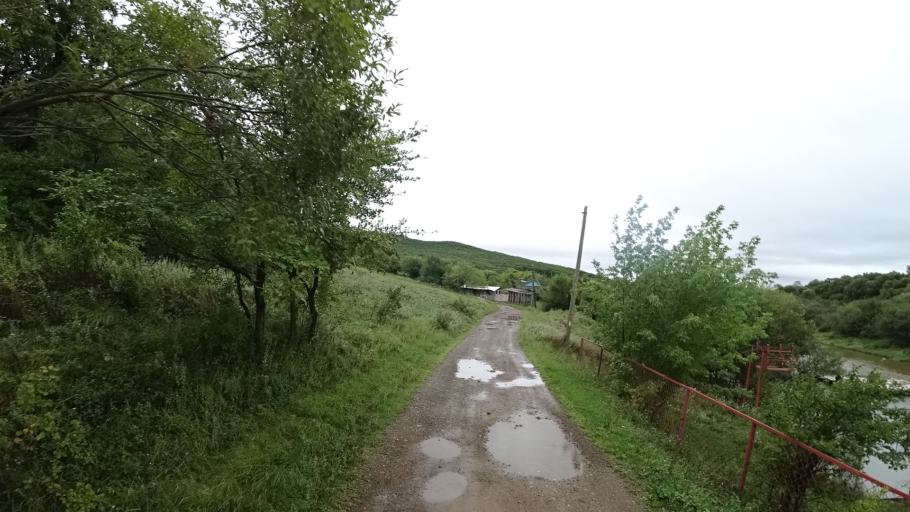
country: RU
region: Primorskiy
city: Monastyrishche
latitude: 44.2741
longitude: 132.4058
